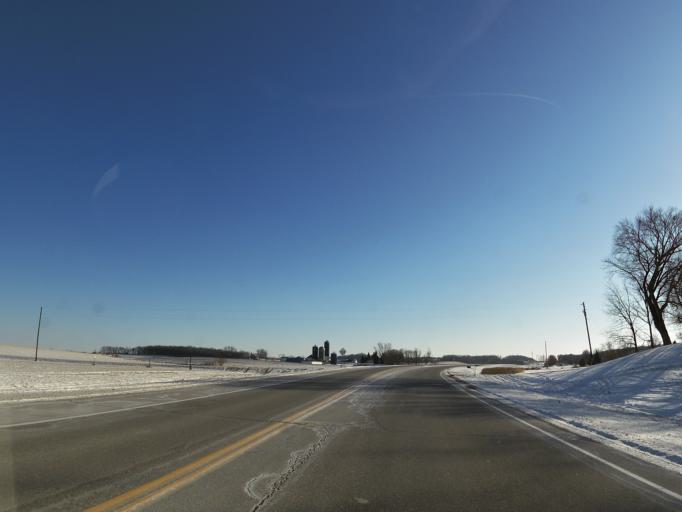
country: US
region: Minnesota
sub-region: Le Sueur County
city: New Prague
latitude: 44.5671
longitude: -93.5025
